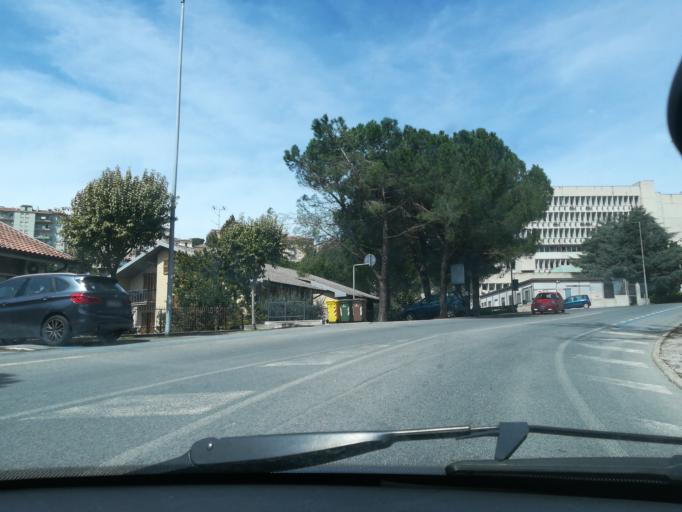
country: IT
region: The Marches
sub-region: Provincia di Macerata
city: Macerata
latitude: 43.2941
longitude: 13.4498
